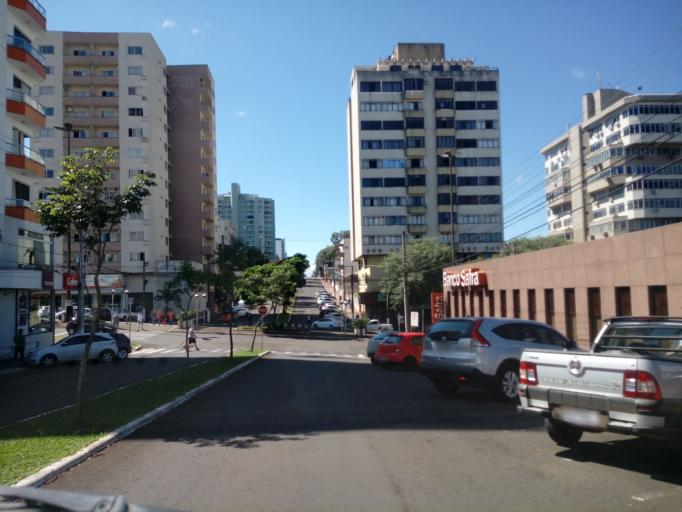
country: BR
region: Santa Catarina
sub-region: Chapeco
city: Chapeco
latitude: -27.0967
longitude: -52.6171
